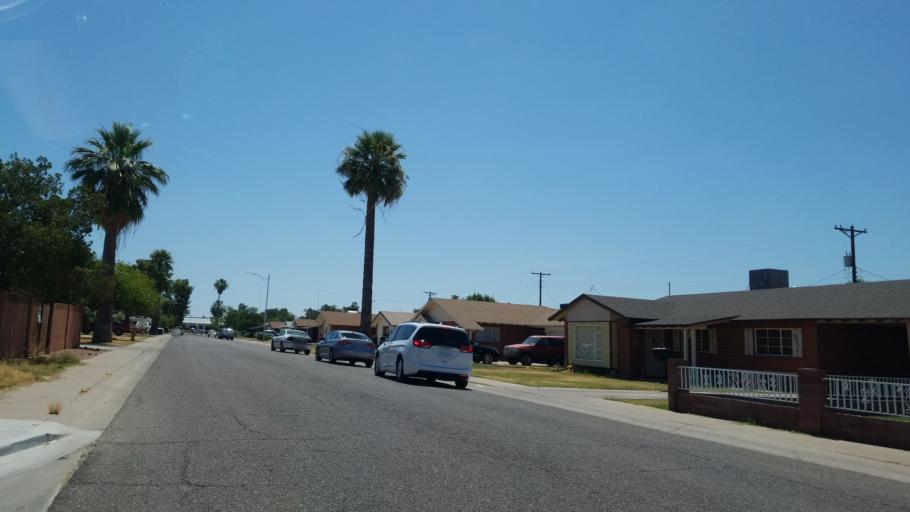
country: US
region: Arizona
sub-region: Maricopa County
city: Glendale
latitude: 33.5363
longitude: -112.1374
